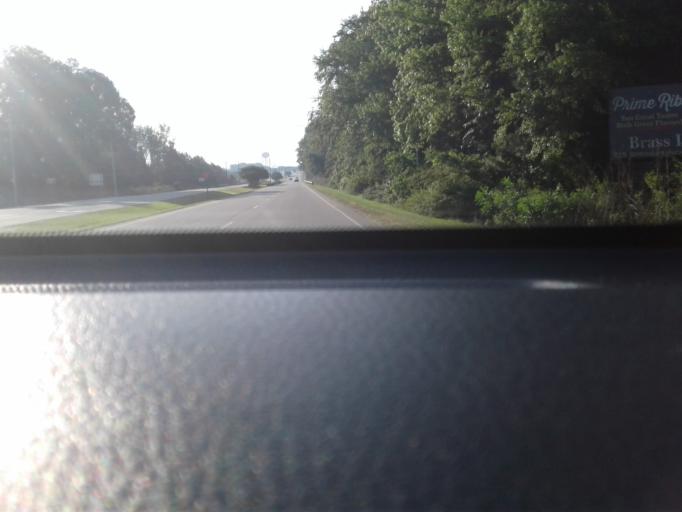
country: US
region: North Carolina
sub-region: Harnett County
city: Erwin
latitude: 35.3231
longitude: -78.6444
